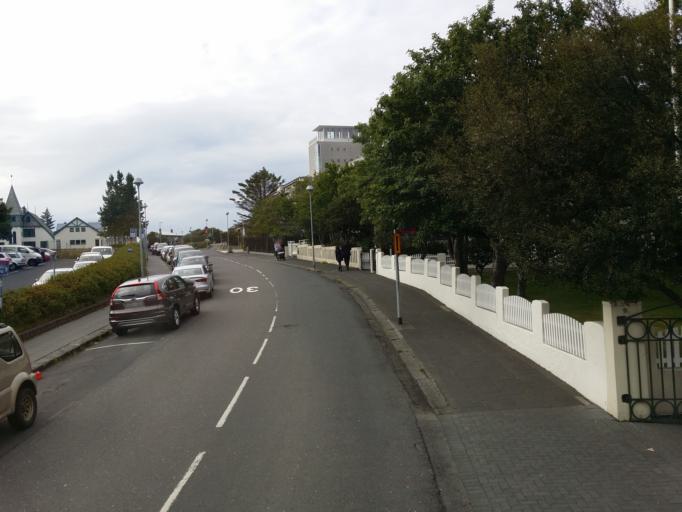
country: IS
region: Capital Region
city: Kopavogur
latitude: 64.1479
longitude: -21.9460
